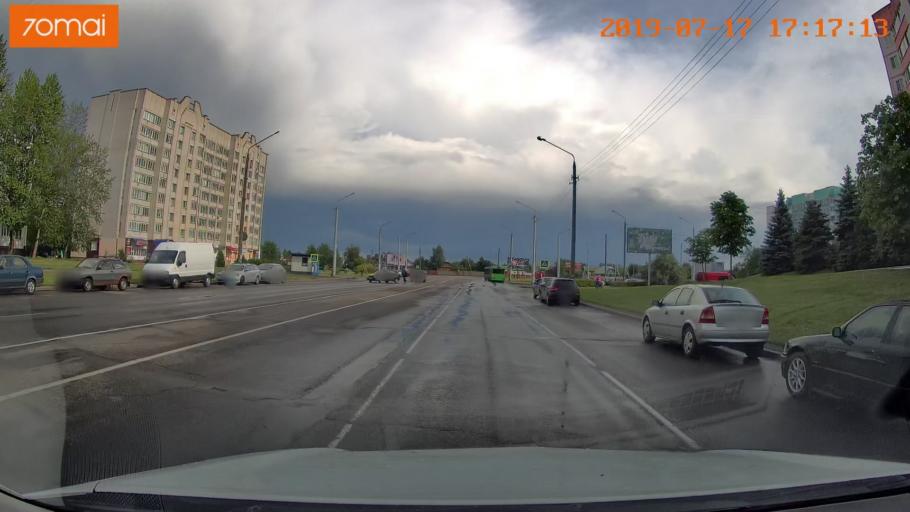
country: BY
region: Mogilev
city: Babruysk
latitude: 53.1618
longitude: 29.1983
